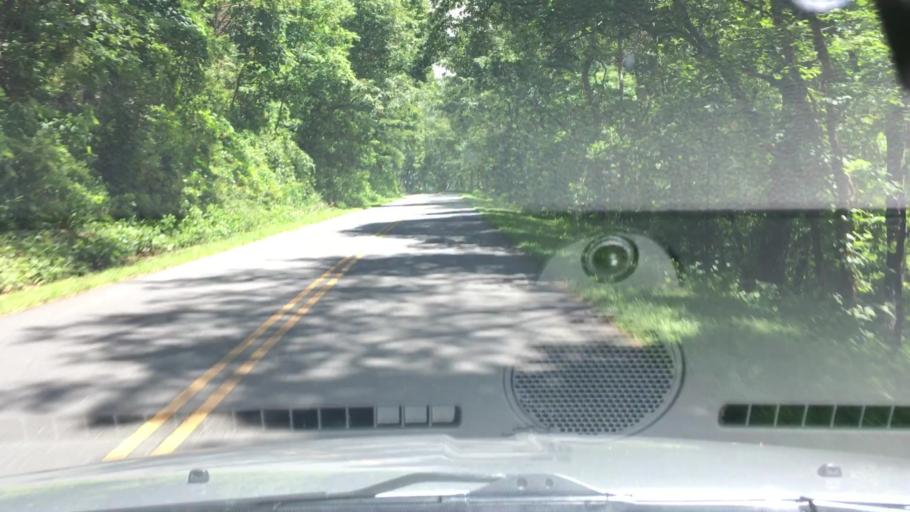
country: US
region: North Carolina
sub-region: Buncombe County
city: Swannanoa
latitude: 35.6678
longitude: -82.4455
